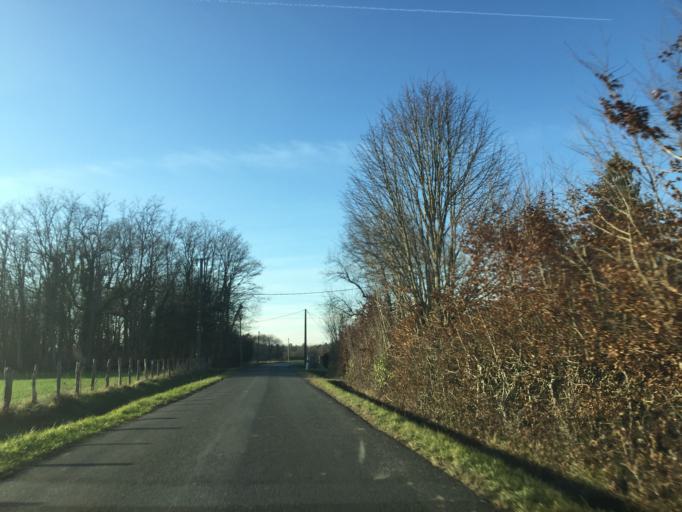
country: FR
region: Aquitaine
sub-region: Departement de la Dordogne
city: Riberac
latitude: 45.2024
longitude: 0.3215
